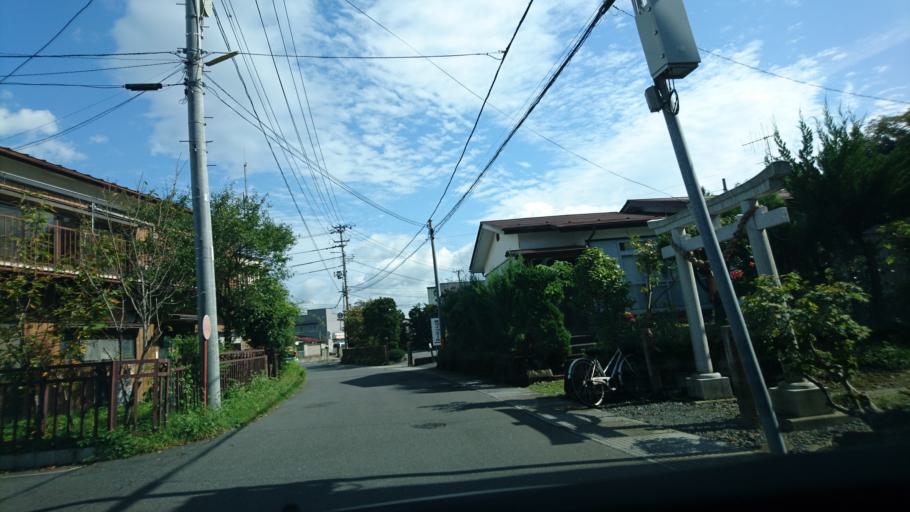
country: JP
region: Iwate
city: Ichinoseki
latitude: 38.9285
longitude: 141.1550
